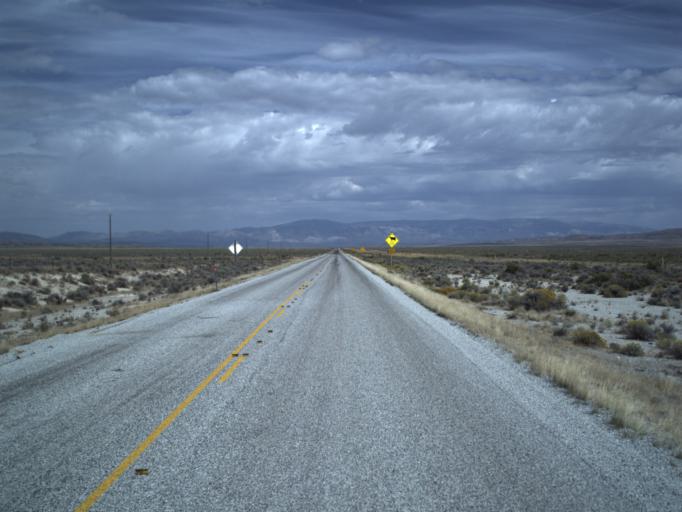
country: US
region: Utah
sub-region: Tooele County
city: Wendover
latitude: 41.5640
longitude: -113.5820
